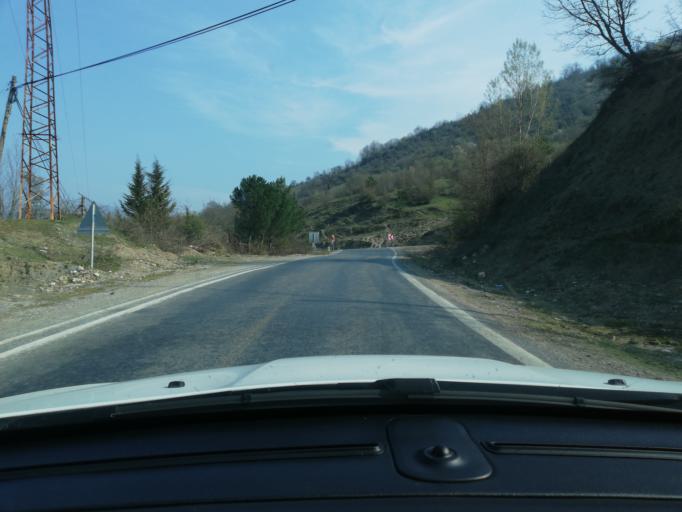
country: TR
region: Karabuk
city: Yenice
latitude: 41.2249
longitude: 32.3621
